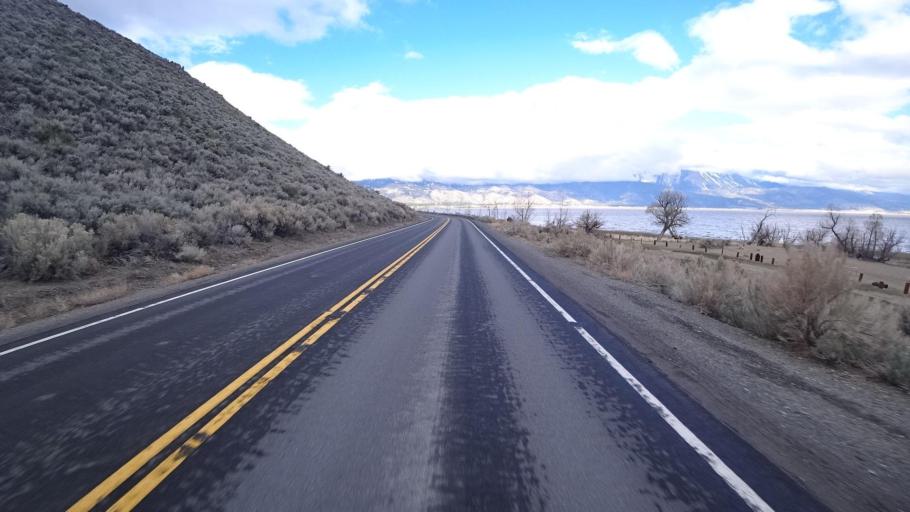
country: US
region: Nevada
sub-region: Carson City
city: Carson City
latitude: 39.2353
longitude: -119.7728
